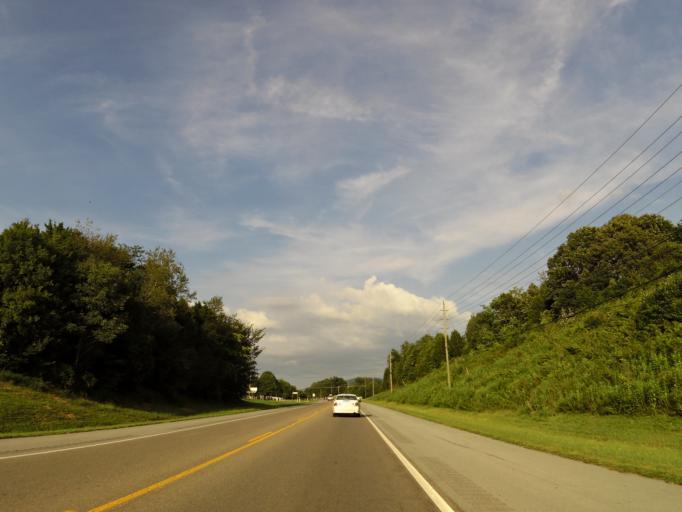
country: US
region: Tennessee
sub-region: Sevier County
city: Sevierville
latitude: 35.8830
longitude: -83.4631
